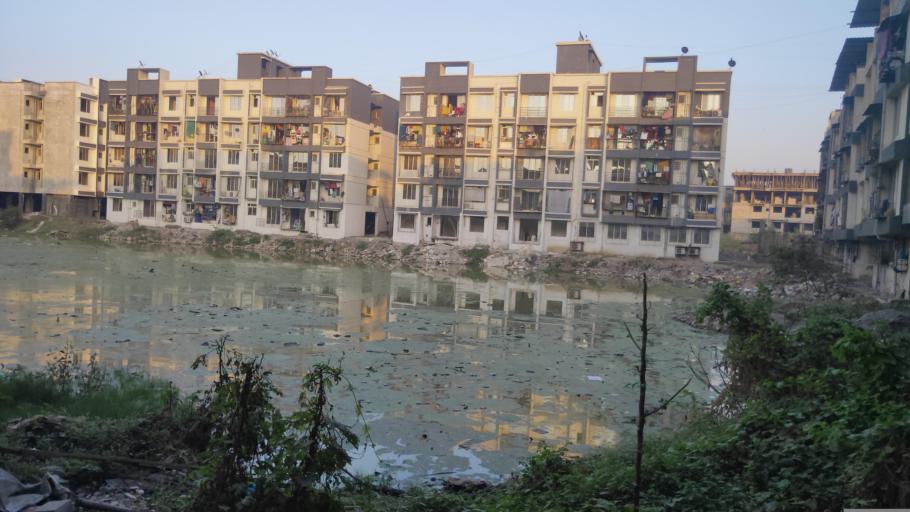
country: IN
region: Maharashtra
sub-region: Thane
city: Thane
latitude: 19.2394
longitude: 73.0112
